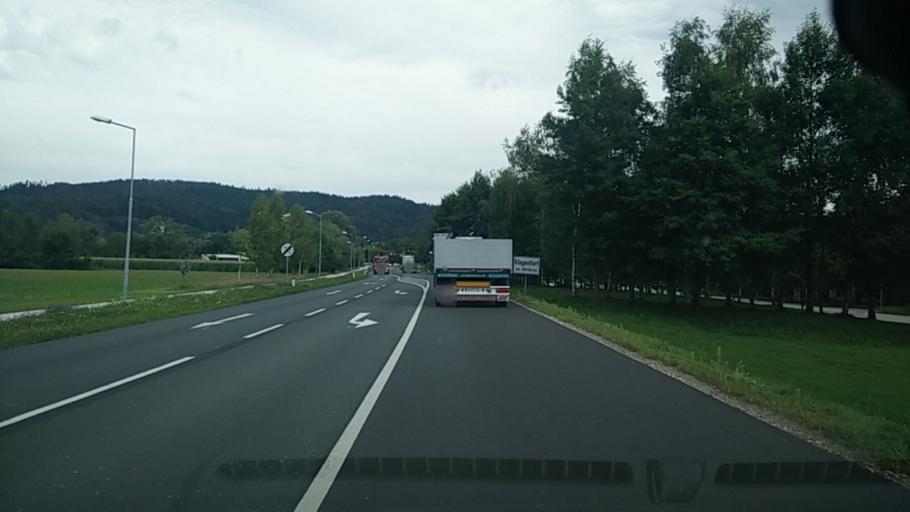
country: AT
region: Carinthia
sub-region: Klagenfurt am Woerthersee
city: Klagenfurt am Woerthersee
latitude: 46.6138
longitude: 14.2612
